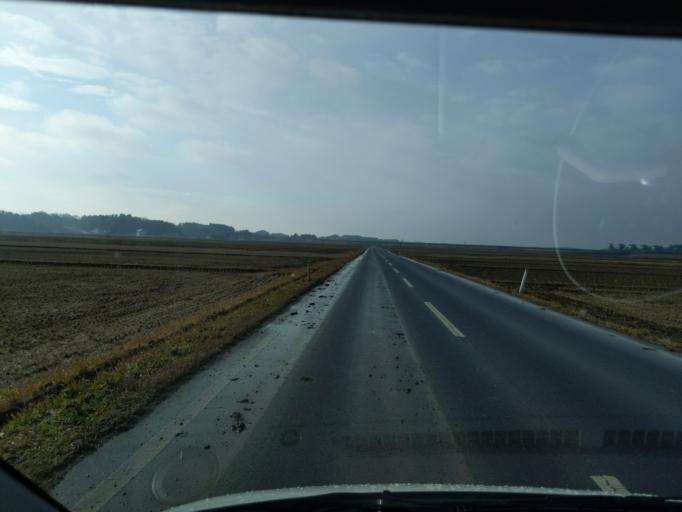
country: JP
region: Miyagi
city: Wakuya
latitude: 38.7176
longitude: 141.1590
